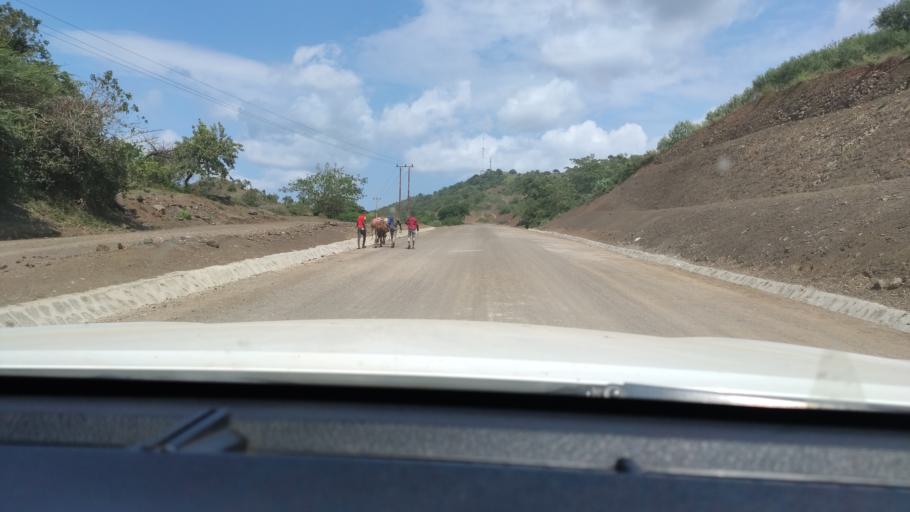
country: ET
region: Southern Nations, Nationalities, and People's Region
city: Felege Neway
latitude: 6.3904
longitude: 37.0645
